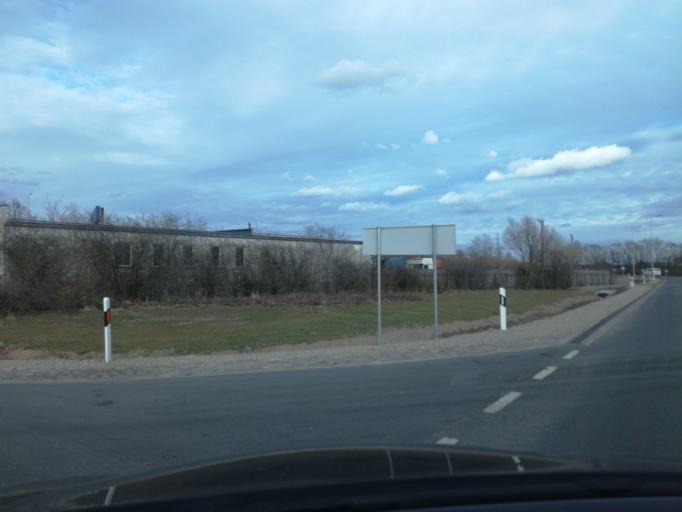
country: LT
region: Marijampoles apskritis
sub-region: Marijampole Municipality
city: Marijampole
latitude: 54.5941
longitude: 23.3941
